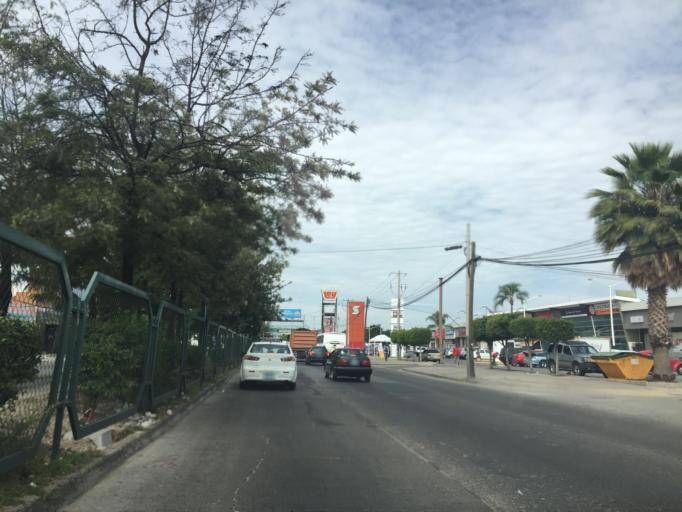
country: MX
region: Guanajuato
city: Leon
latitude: 21.0991
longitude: -101.6691
